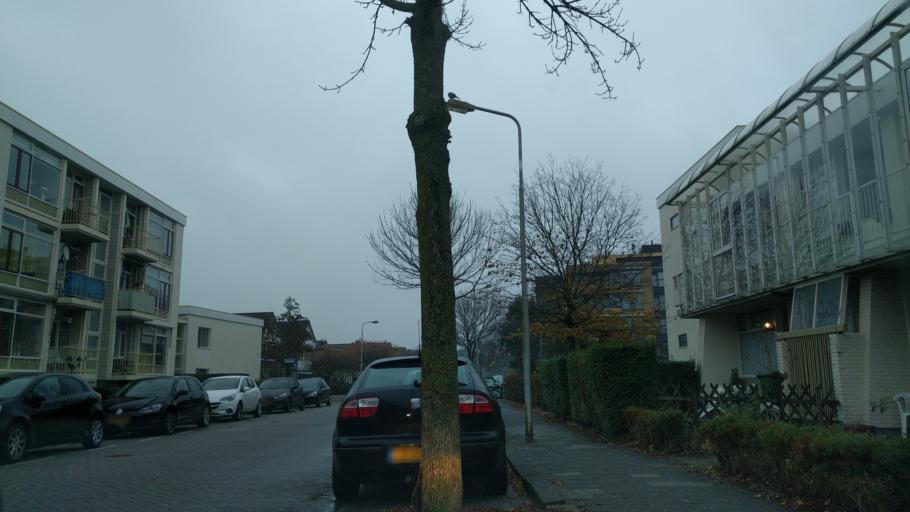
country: NL
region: South Holland
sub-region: Gemeente Capelle aan den IJssel
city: Capelle-West
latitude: 51.8942
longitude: 4.5787
